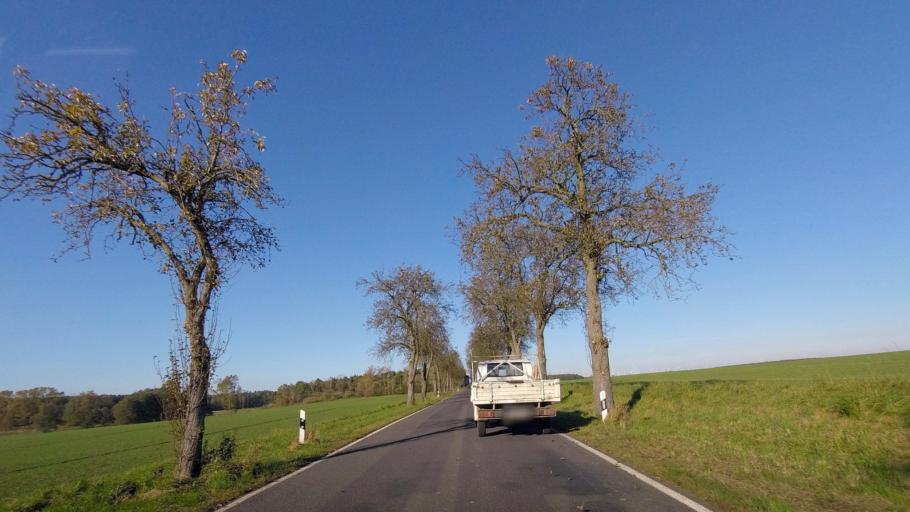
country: DE
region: Saxony-Anhalt
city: Zahna
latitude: 51.9516
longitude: 12.7857
